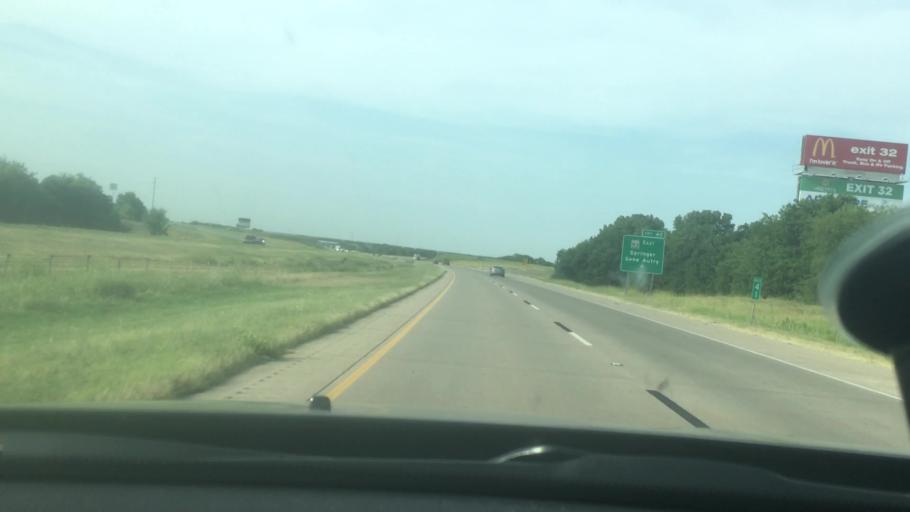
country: US
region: Oklahoma
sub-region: Carter County
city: Ardmore
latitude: 34.3086
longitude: -97.1594
